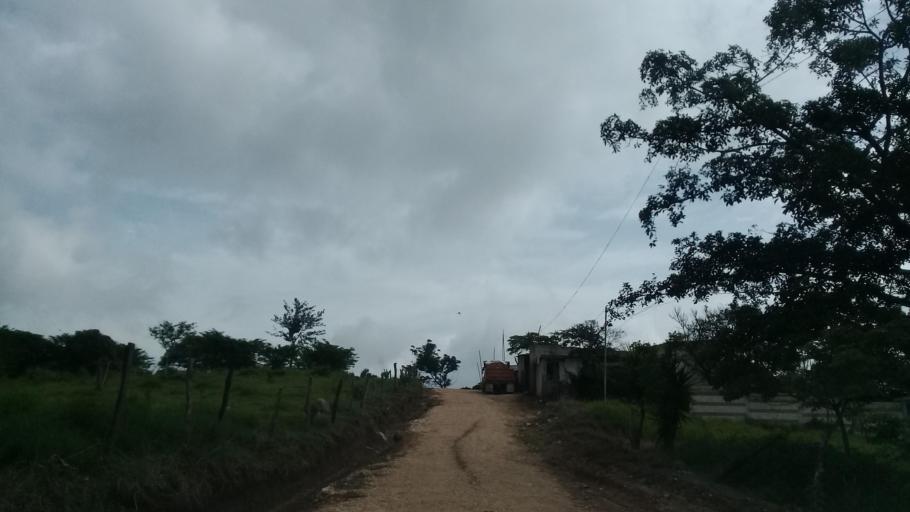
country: MX
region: Veracruz
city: El Castillo
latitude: 19.5514
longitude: -96.8766
